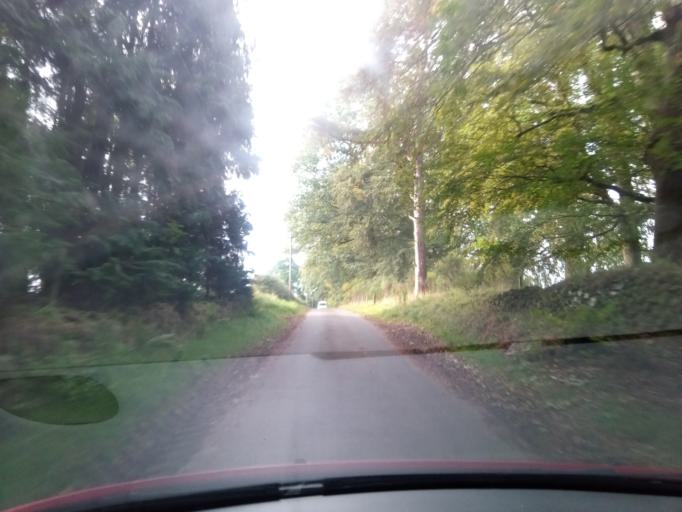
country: GB
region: Scotland
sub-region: The Scottish Borders
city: Kelso
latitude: 55.5930
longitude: -2.3926
